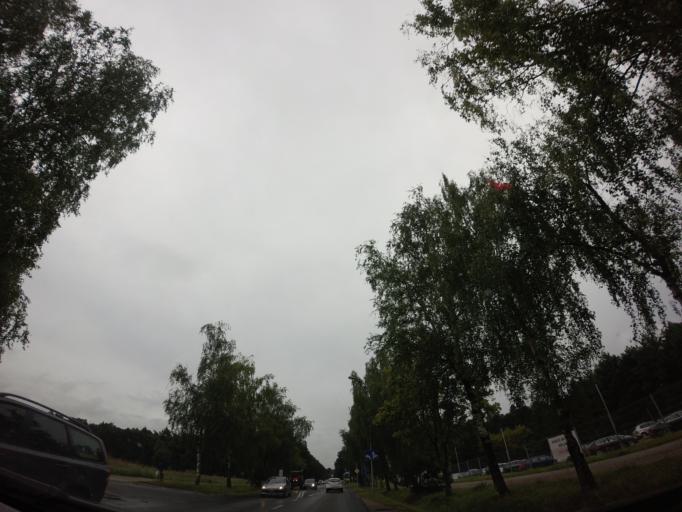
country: PL
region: Greater Poland Voivodeship
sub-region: Powiat poznanski
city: Baranowo
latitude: 52.4179
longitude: 16.7891
